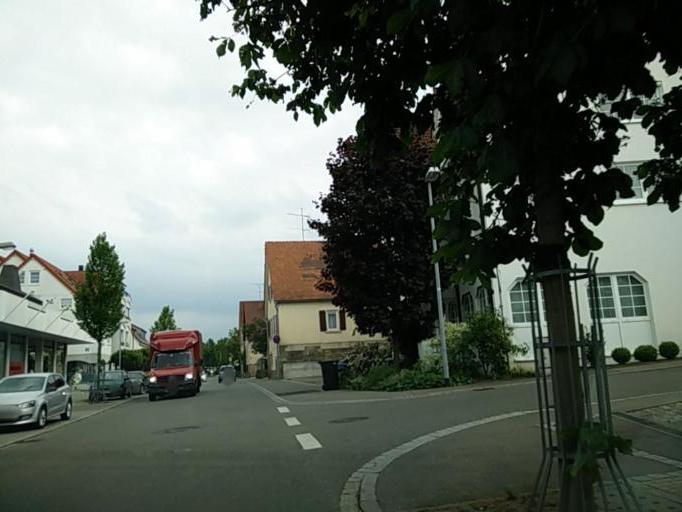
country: DE
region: Baden-Wuerttemberg
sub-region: Regierungsbezirk Stuttgart
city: Holzgerlingen
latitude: 48.6350
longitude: 9.0128
